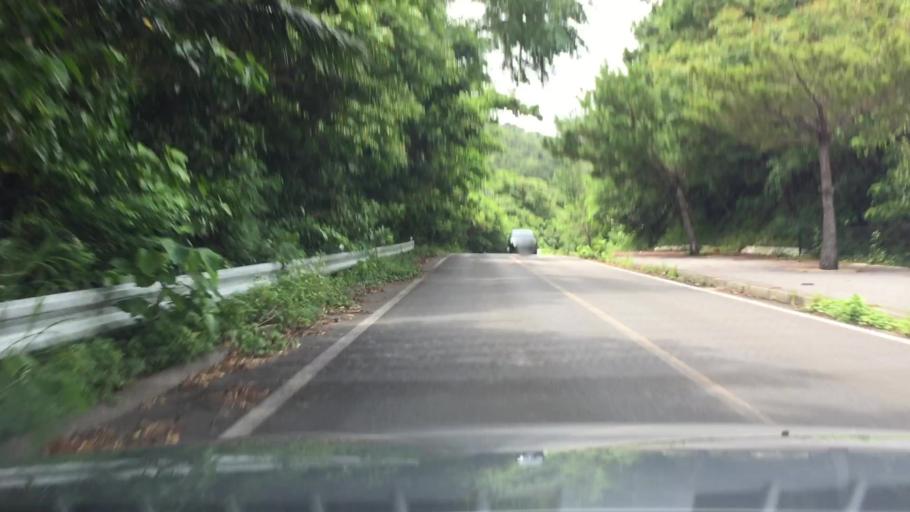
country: JP
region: Okinawa
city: Ishigaki
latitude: 24.4263
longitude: 124.2113
